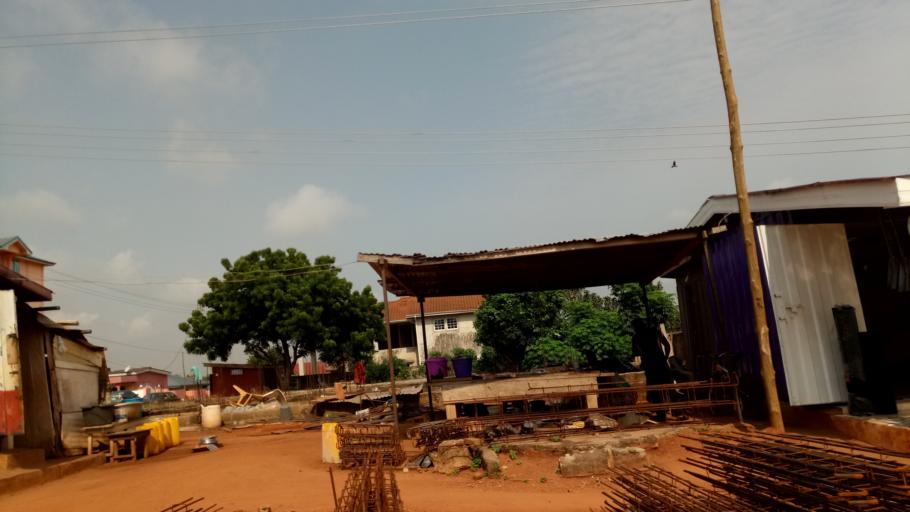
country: GH
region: Greater Accra
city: Medina Estates
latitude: 5.6738
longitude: -0.1908
